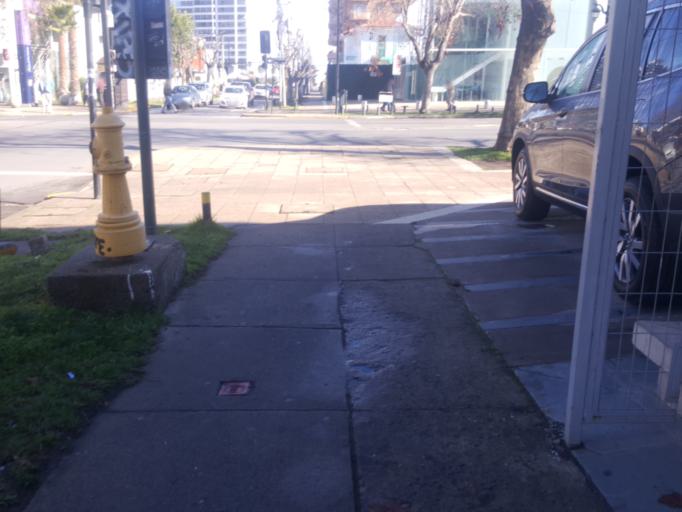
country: CL
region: Valparaiso
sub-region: Provincia de Valparaiso
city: Vina del Mar
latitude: -33.0112
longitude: -71.5487
